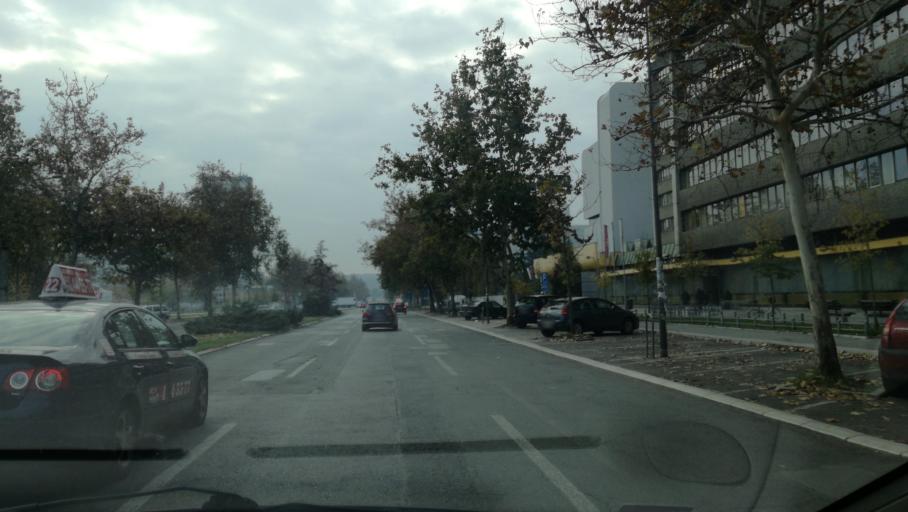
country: RS
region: Autonomna Pokrajina Vojvodina
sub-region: Juznobacki Okrug
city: Novi Sad
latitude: 45.2460
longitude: 19.8402
